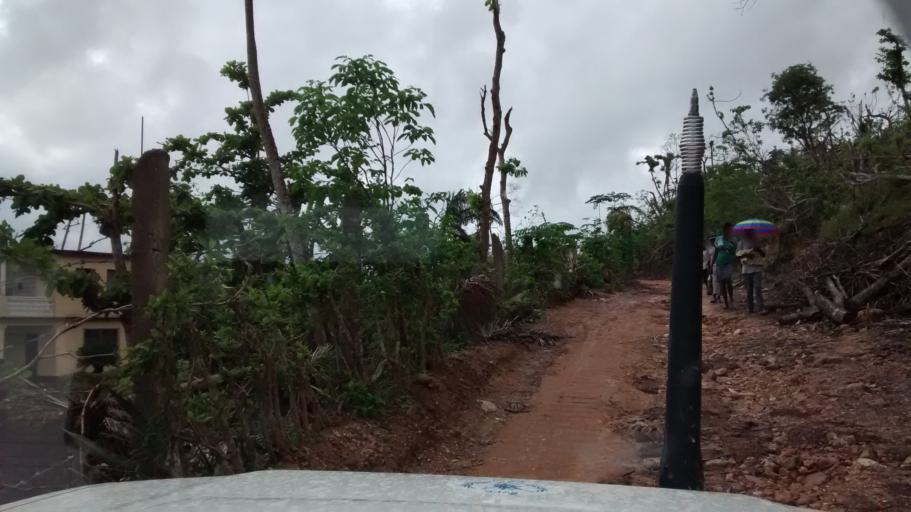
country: HT
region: Grandans
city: Jeremie
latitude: 18.5951
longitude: -74.1383
